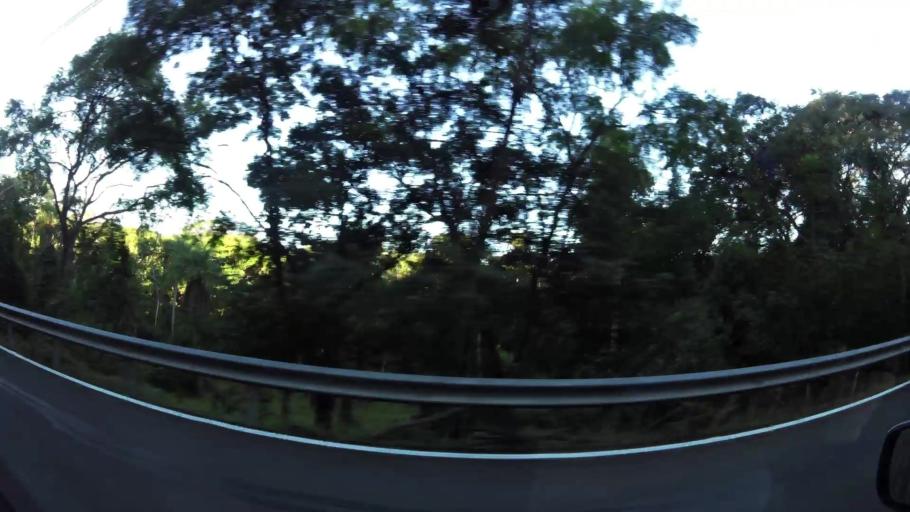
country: CR
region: Puntarenas
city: Miramar
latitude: 10.1738
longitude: -84.8491
